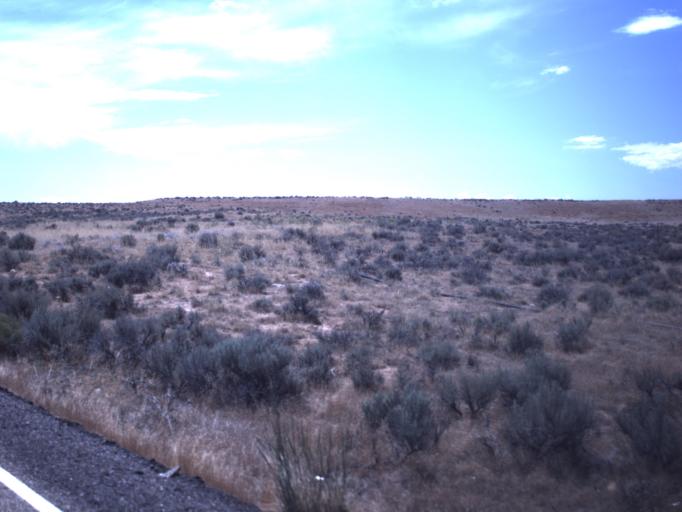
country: US
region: Utah
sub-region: Uintah County
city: Maeser
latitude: 40.2943
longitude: -109.6863
